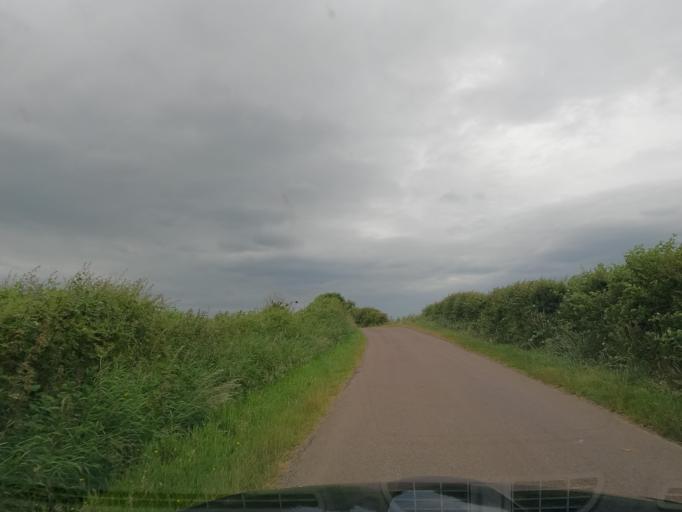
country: GB
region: England
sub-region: Northumberland
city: Ancroft
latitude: 55.6700
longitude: -2.0322
